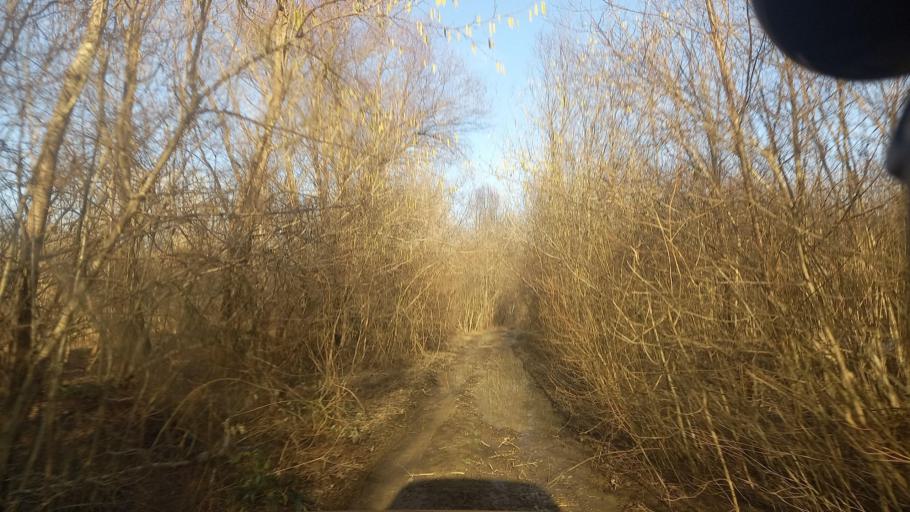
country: RU
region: Krasnodarskiy
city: Smolenskaya
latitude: 44.6817
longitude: 38.7840
